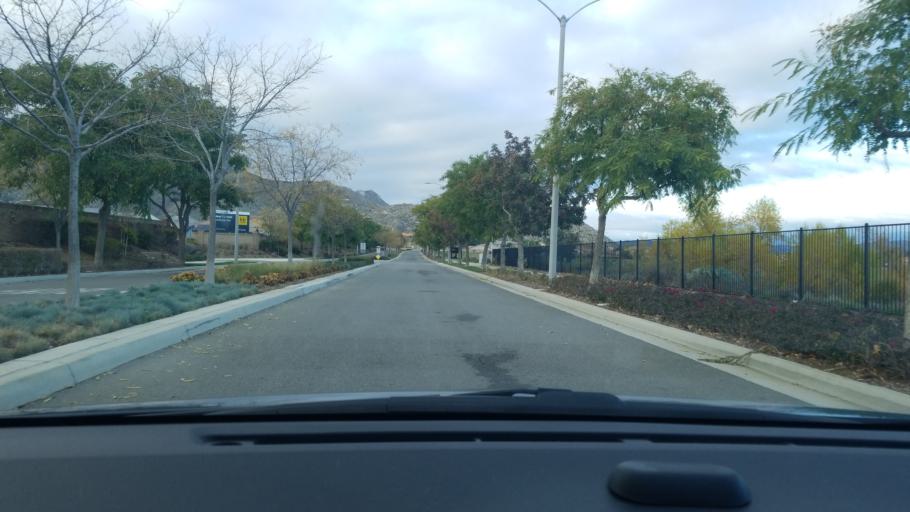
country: US
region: California
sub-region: Riverside County
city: Green Acres
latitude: 33.7898
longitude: -117.0363
